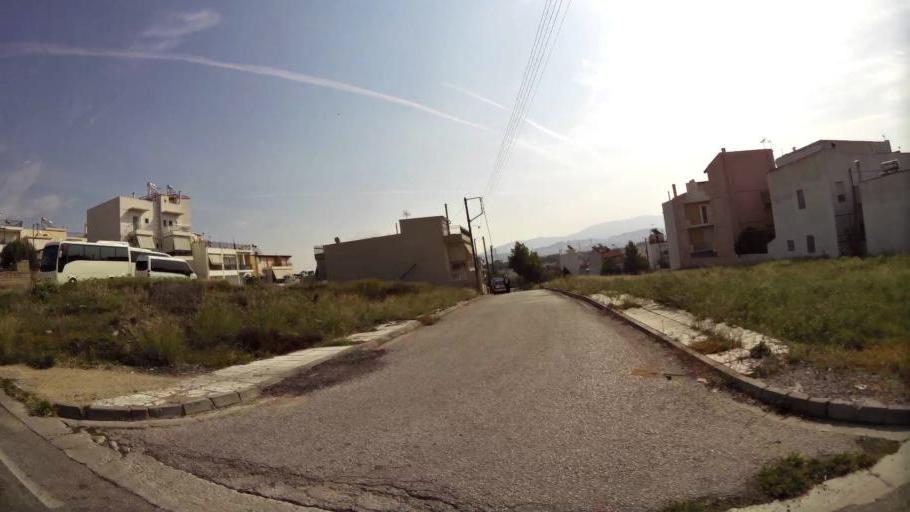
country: GR
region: Attica
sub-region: Nomarchia Athinas
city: Kamateron
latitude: 38.0486
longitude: 23.7093
